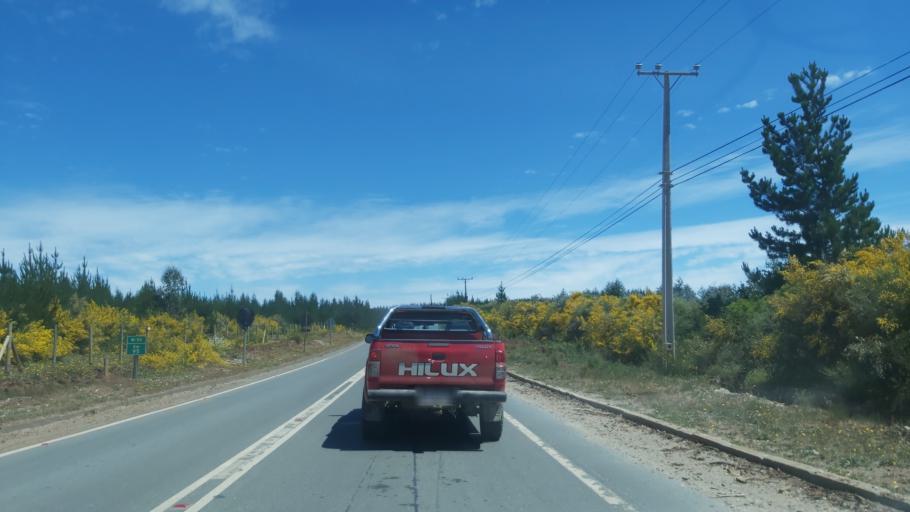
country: CL
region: Maule
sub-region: Provincia de Talca
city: Constitucion
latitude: -35.4053
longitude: -72.4380
